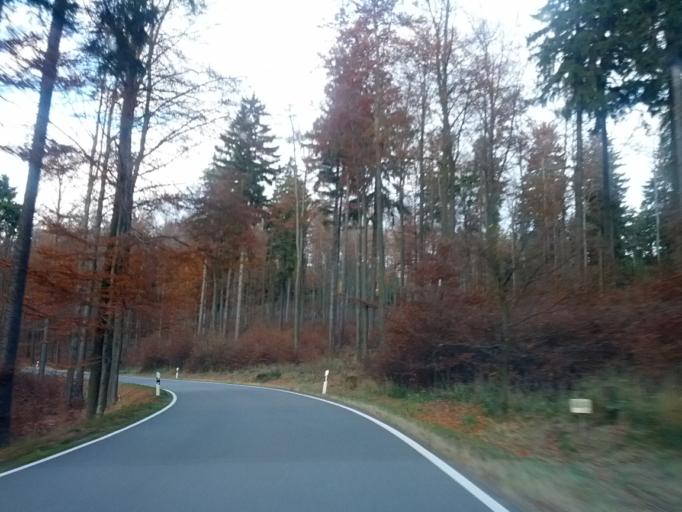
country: DE
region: Thuringia
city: Brotterode
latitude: 50.8420
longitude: 10.4069
